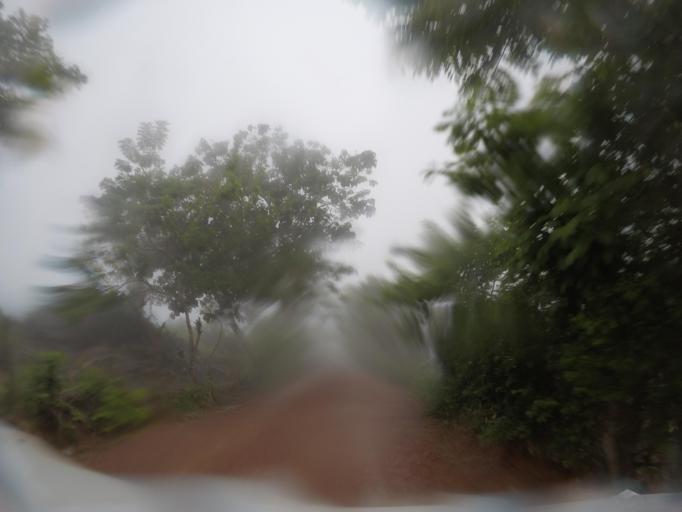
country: TL
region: Baucau
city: Venilale
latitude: -8.6363
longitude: 126.4206
